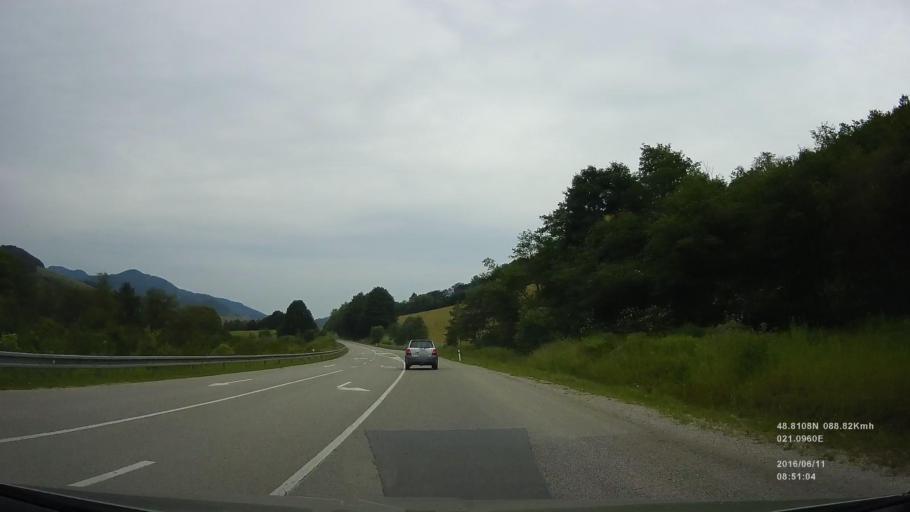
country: SK
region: Kosicky
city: Gelnica
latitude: 48.8039
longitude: 21.1015
